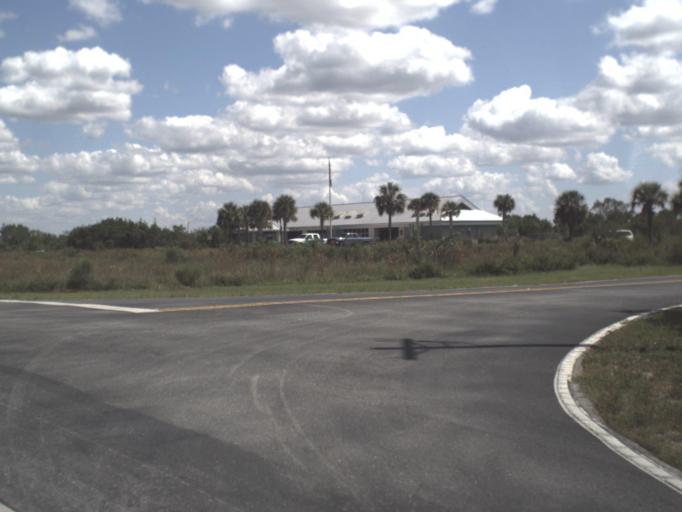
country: US
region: Florida
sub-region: Collier County
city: Marco
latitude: 25.9013
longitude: -81.3269
